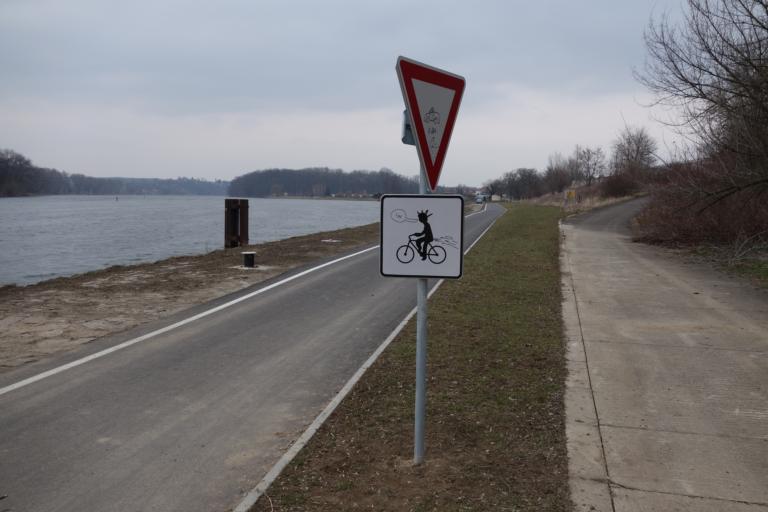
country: CZ
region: Ustecky
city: Roudnice nad Labem
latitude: 50.4332
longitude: 14.2872
